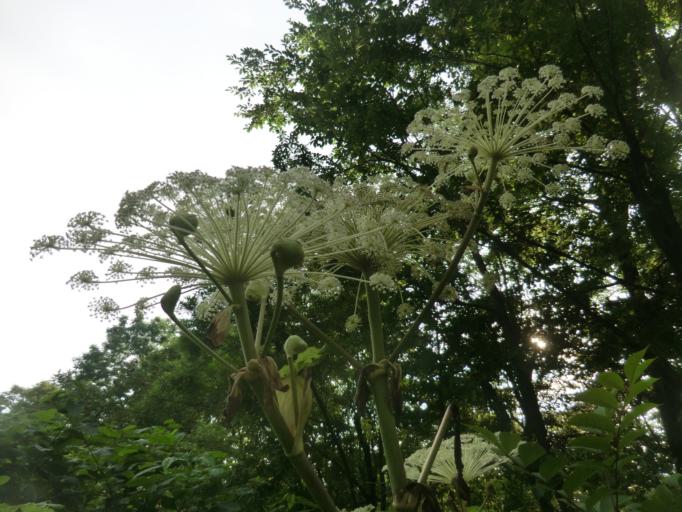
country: JP
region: Hokkaido
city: Nayoro
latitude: 44.3968
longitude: 142.2061
